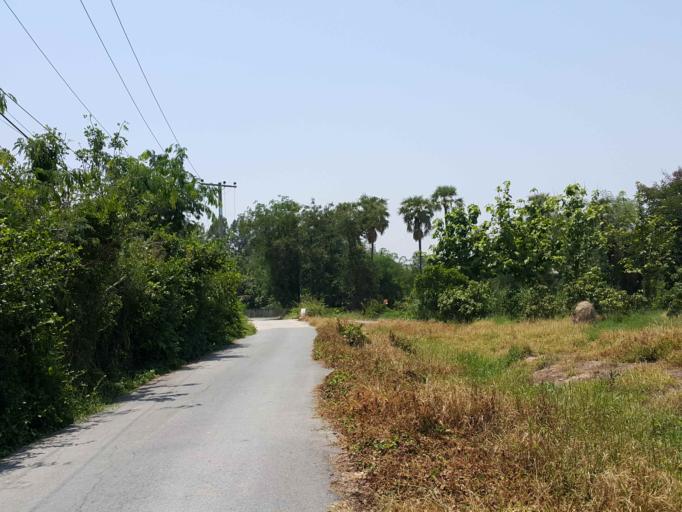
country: TH
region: Chiang Mai
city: San Sai
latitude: 18.8255
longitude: 99.1067
